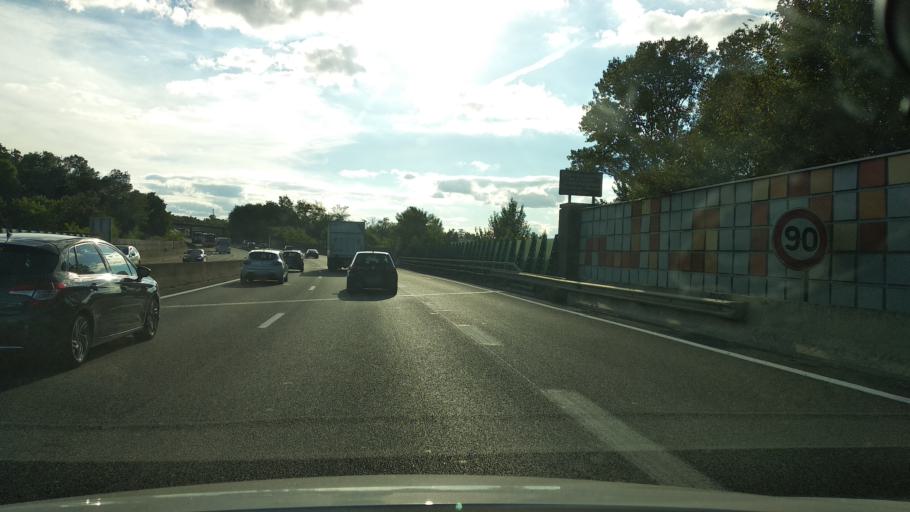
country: FR
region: Midi-Pyrenees
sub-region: Departement du Tarn-et-Garonne
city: Montauban
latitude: 44.0010
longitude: 1.3680
